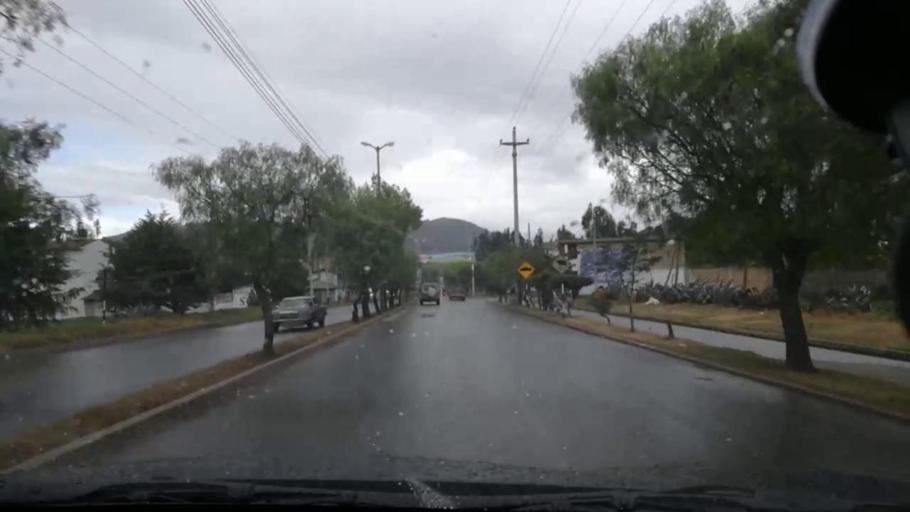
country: PE
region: Cajamarca
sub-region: Provincia de Cajamarca
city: Cajamarca
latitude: -7.1652
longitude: -78.4815
